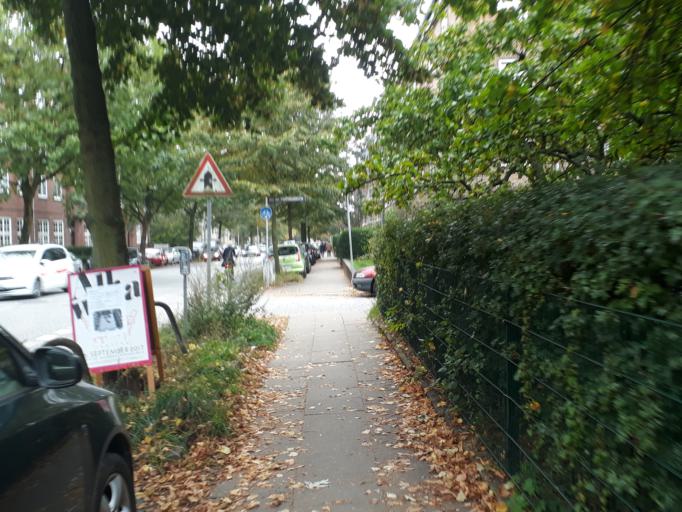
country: DE
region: Hamburg
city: Hamburg
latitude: 53.5886
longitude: 10.0105
